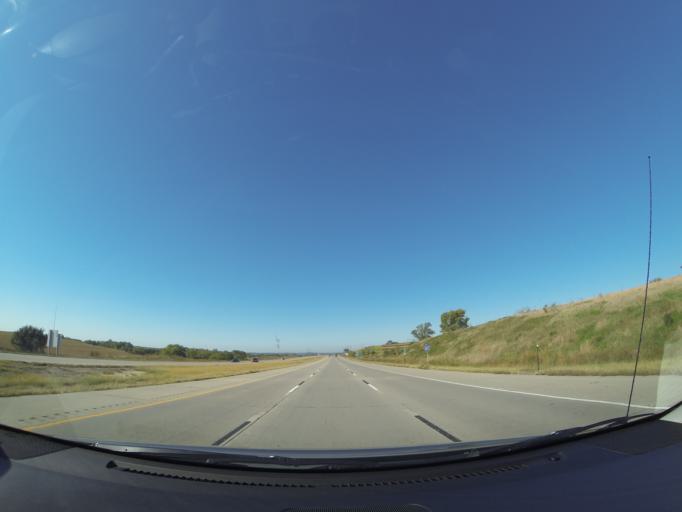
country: US
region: Nebraska
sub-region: Sarpy County
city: Gretna
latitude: 41.0907
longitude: -96.2617
